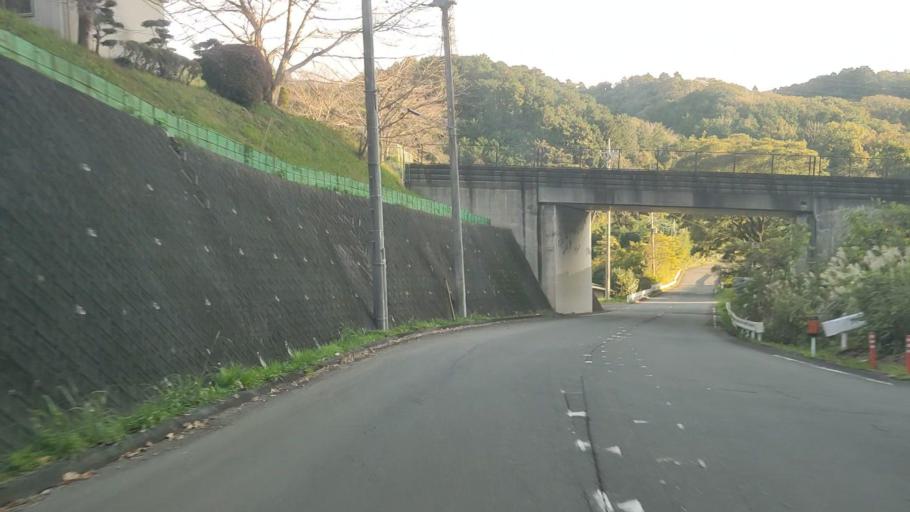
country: JP
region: Shizuoka
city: Mishima
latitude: 35.1524
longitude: 138.9398
